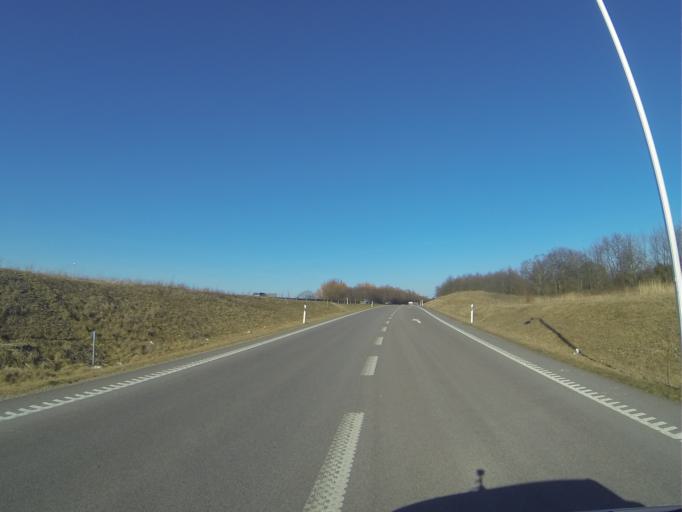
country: SE
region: Skane
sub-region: Lunds Kommun
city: Lund
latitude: 55.6876
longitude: 13.2007
